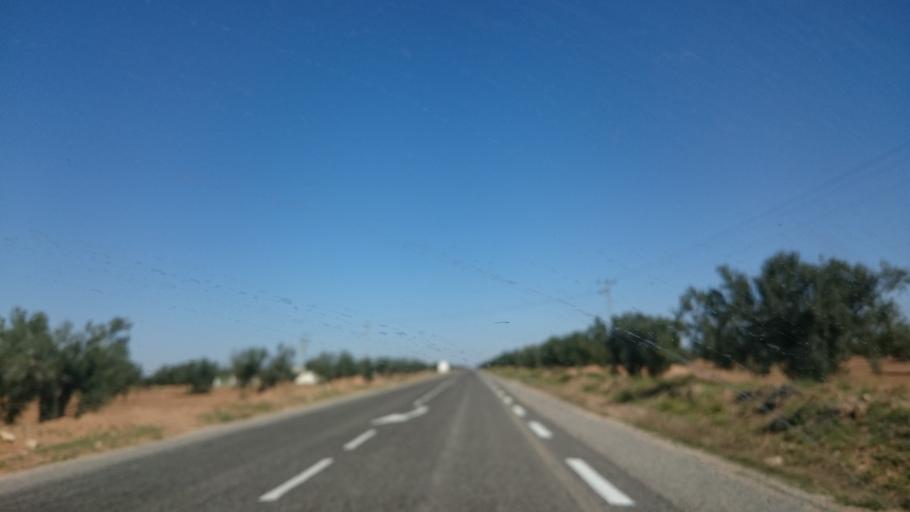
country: TN
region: Safaqis
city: Sfax
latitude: 34.8369
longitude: 10.4604
